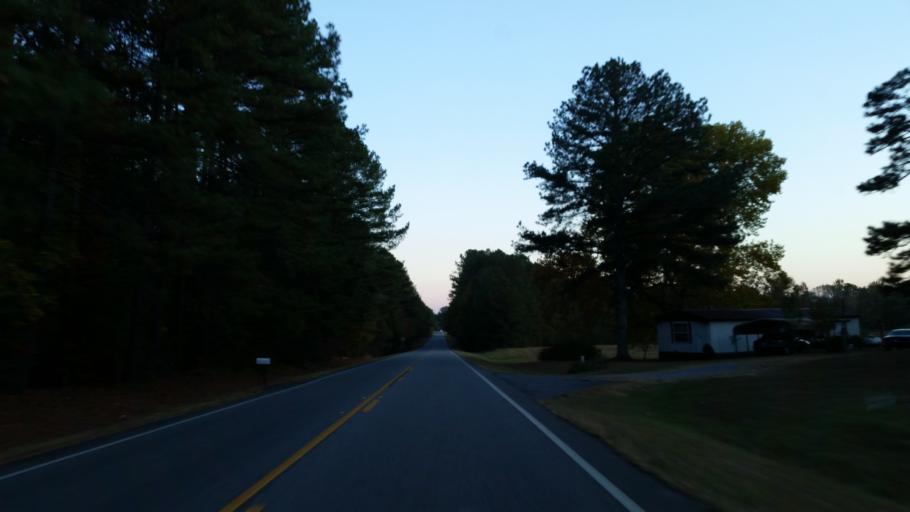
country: US
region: Georgia
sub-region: Gordon County
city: Calhoun
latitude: 34.6056
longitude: -85.0387
